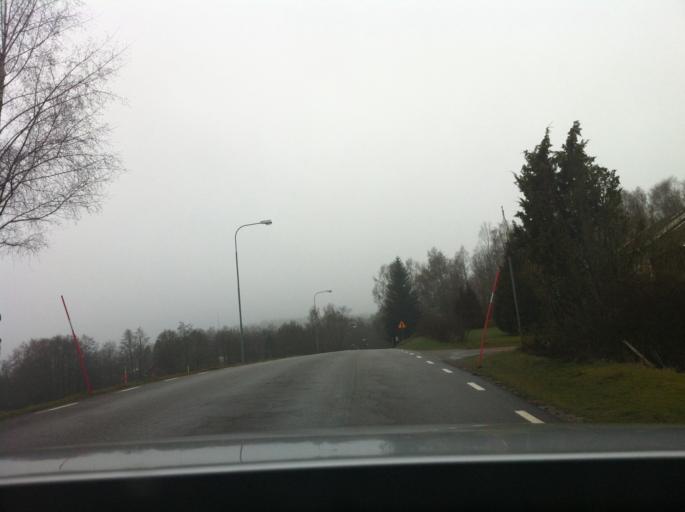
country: SE
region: Vaestra Goetaland
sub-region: Svenljunga Kommun
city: Svenljunga
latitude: 57.2488
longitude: 12.9793
